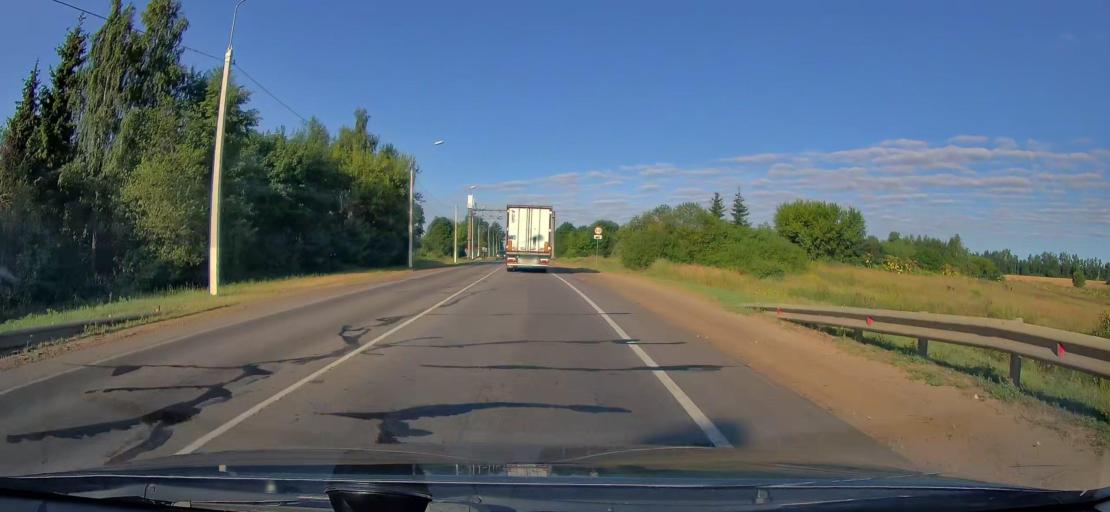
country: RU
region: Tula
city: Bol'shoye Skuratovo
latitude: 53.4545
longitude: 36.8662
